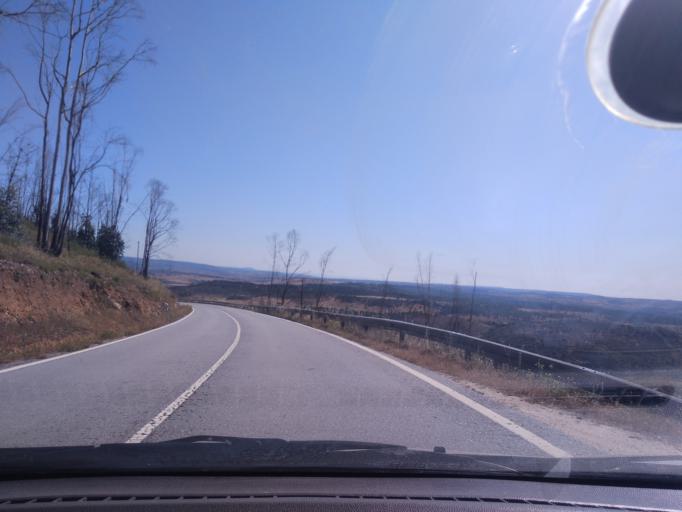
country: PT
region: Portalegre
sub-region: Nisa
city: Nisa
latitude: 39.6254
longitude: -7.6638
